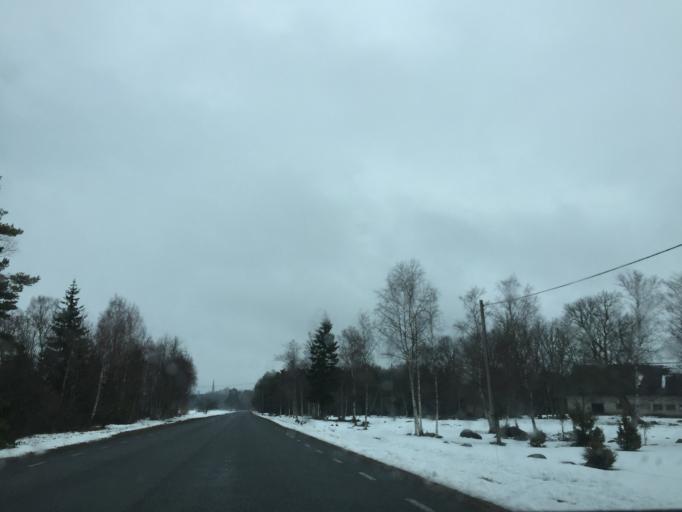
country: EE
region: Saare
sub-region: Kuressaare linn
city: Kuressaare
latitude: 58.3477
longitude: 22.0319
